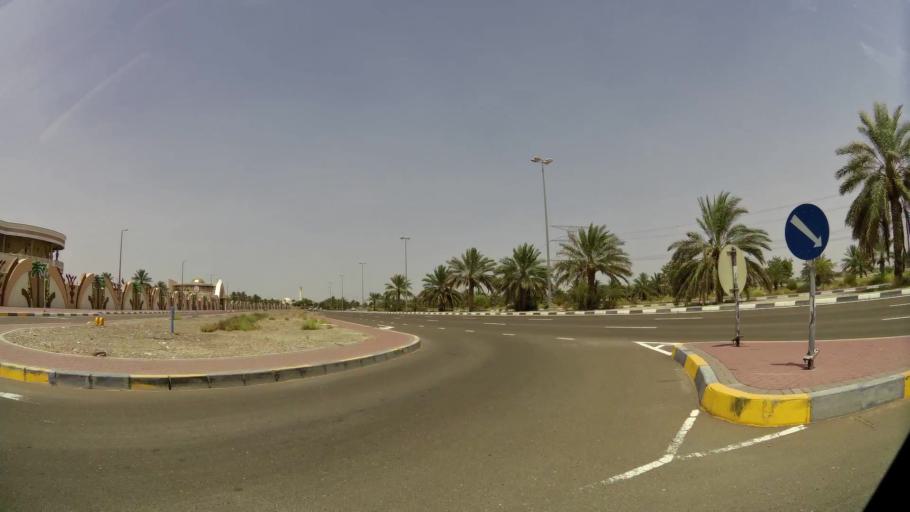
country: AE
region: Abu Dhabi
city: Al Ain
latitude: 24.1815
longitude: 55.6731
